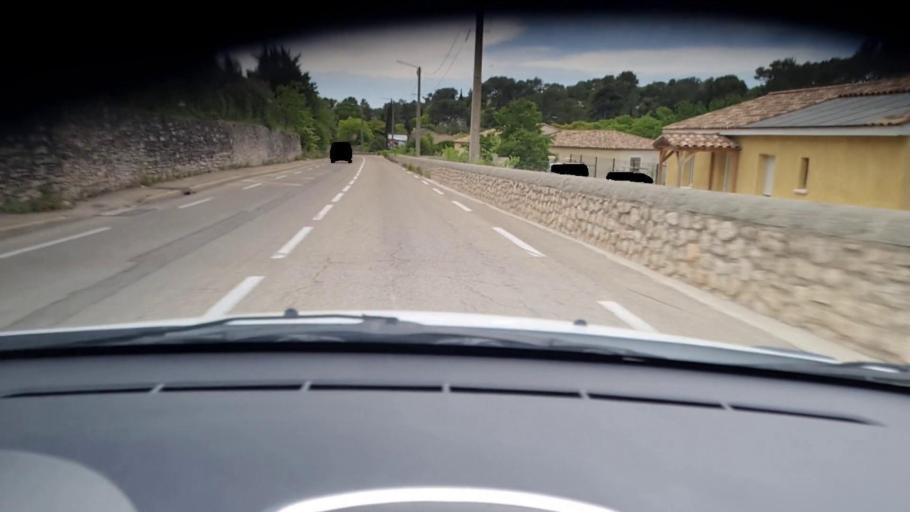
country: FR
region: Languedoc-Roussillon
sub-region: Departement du Gard
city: Nimes
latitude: 43.8626
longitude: 4.3770
